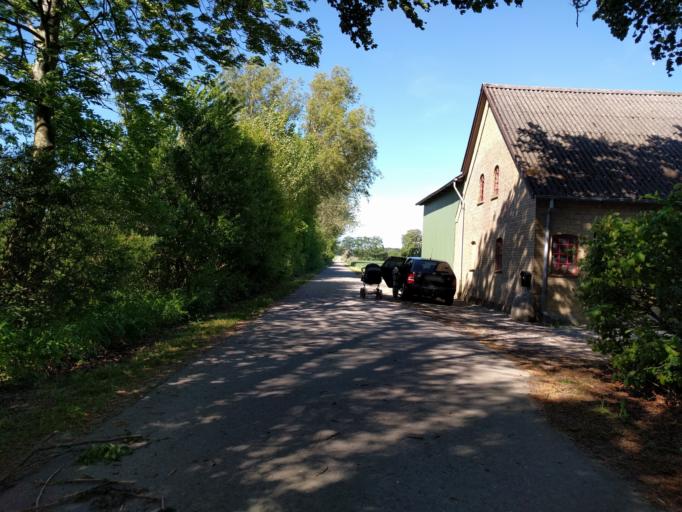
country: DK
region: South Denmark
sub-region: Kerteminde Kommune
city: Kerteminde
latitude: 55.4259
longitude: 10.6614
